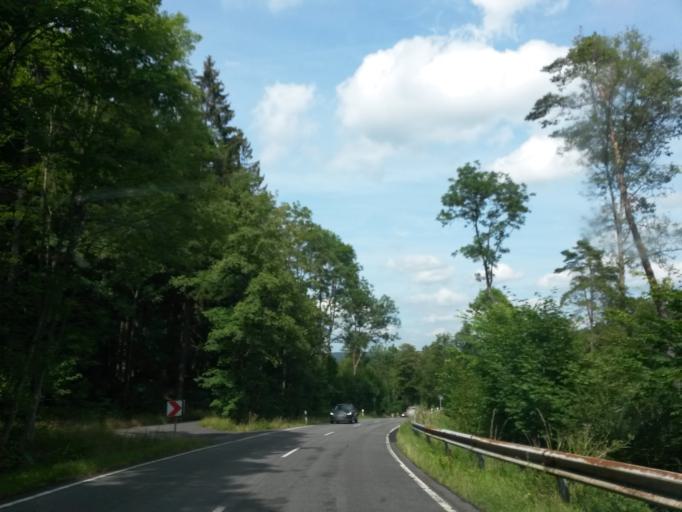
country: DE
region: North Rhine-Westphalia
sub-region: Regierungsbezirk Arnsberg
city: Burbach
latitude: 50.7340
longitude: 8.0742
